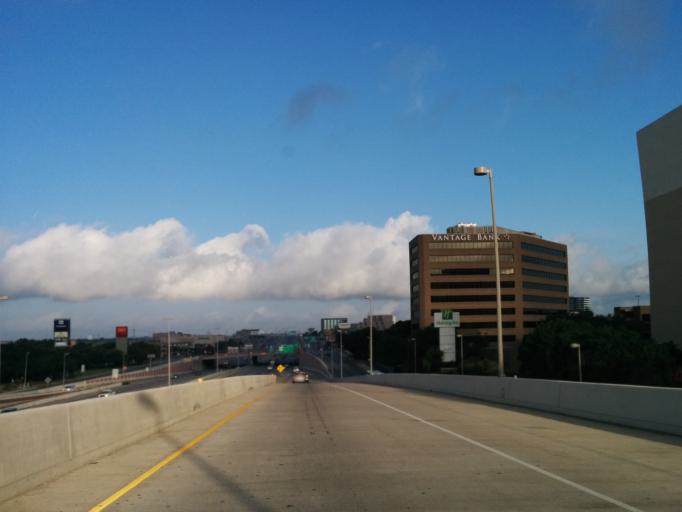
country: US
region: Texas
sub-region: Bexar County
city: Castle Hills
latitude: 29.5206
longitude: -98.4878
